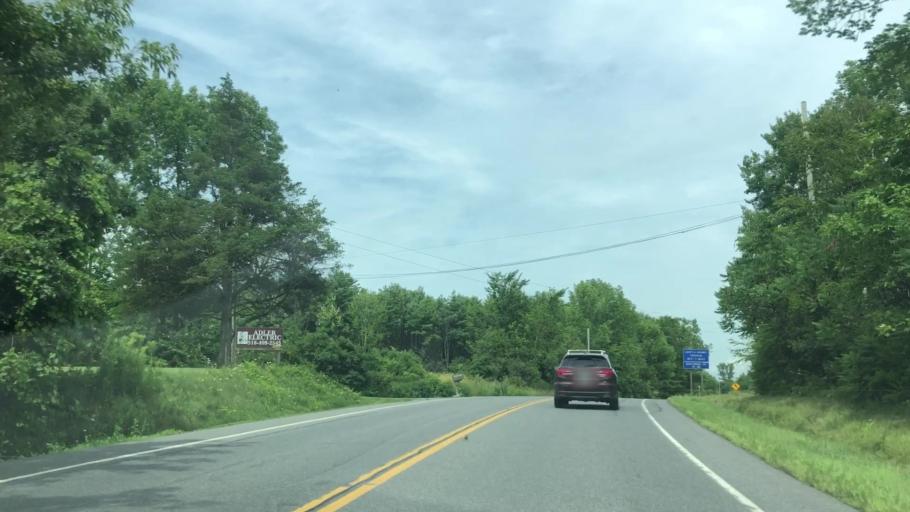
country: US
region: New York
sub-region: Washington County
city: Whitehall
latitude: 43.5016
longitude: -73.4238
